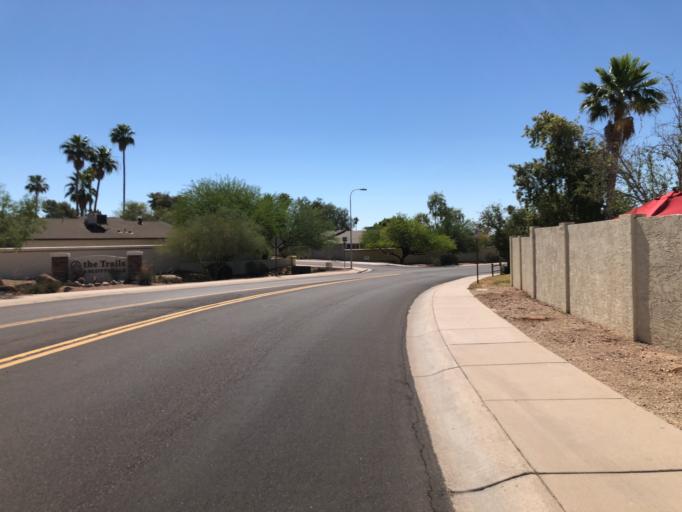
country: US
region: Arizona
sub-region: Maricopa County
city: Tempe
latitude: 33.4584
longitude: -111.8962
